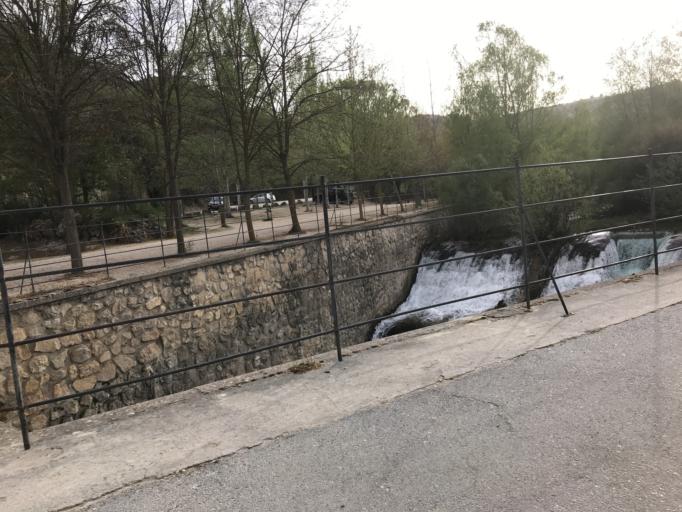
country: ES
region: Andalusia
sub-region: Provincia de Granada
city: Castril
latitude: 37.7959
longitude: -2.7834
